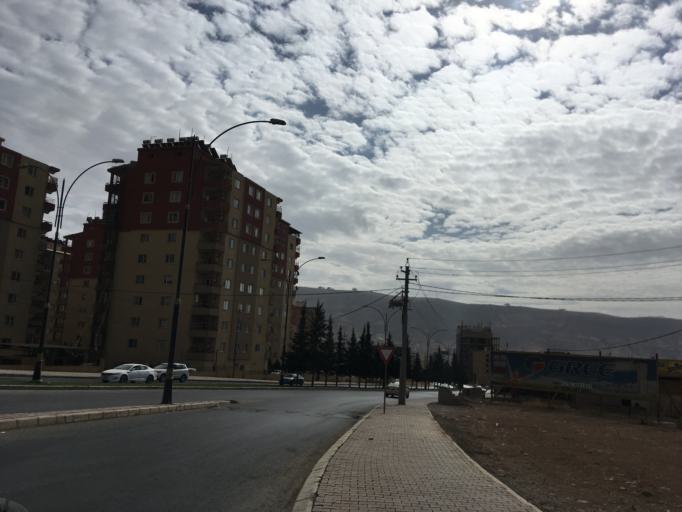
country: IQ
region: Dahuk
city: Dihok
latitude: 36.8672
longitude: 42.9776
